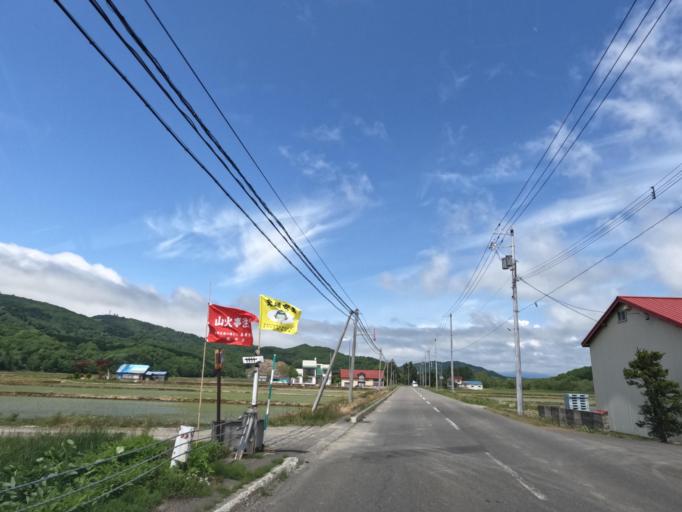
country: JP
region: Hokkaido
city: Tobetsu
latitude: 43.2848
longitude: 141.5370
